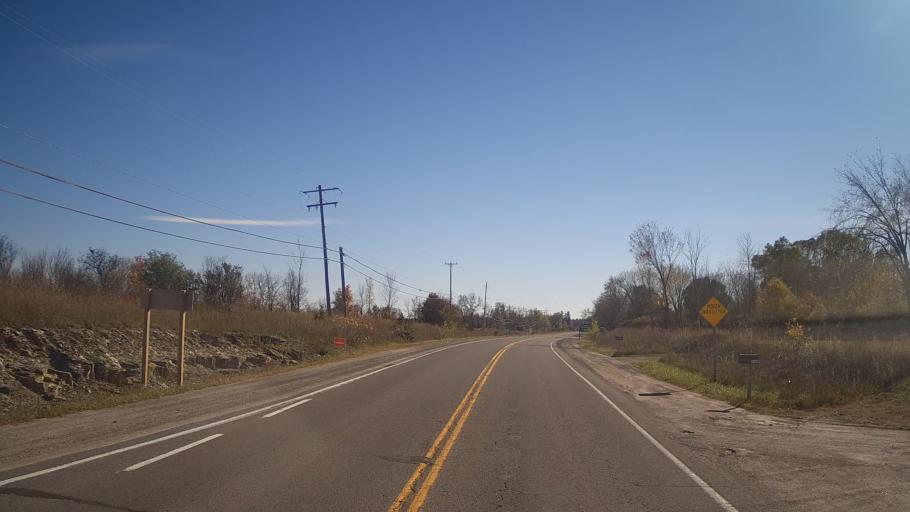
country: CA
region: Ontario
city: Kingston
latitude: 44.4160
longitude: -76.6667
